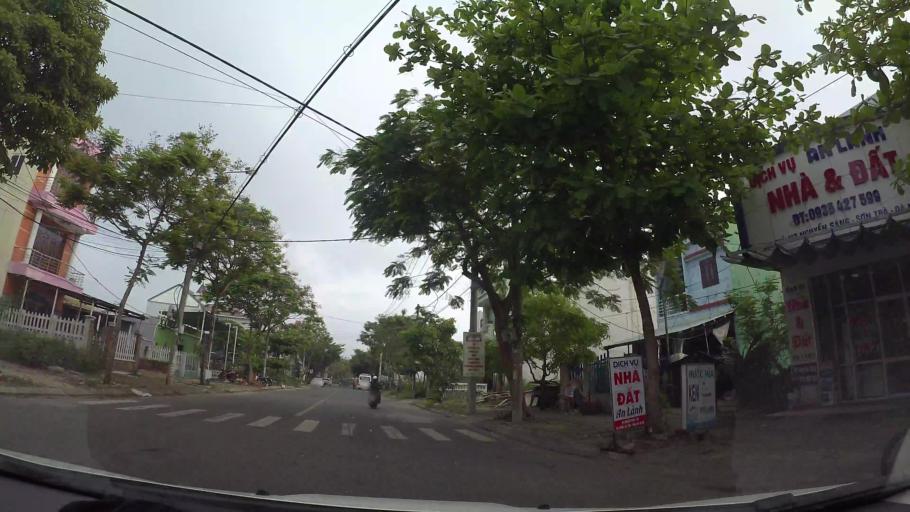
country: VN
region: Da Nang
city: Son Tra
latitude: 16.0856
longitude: 108.2464
